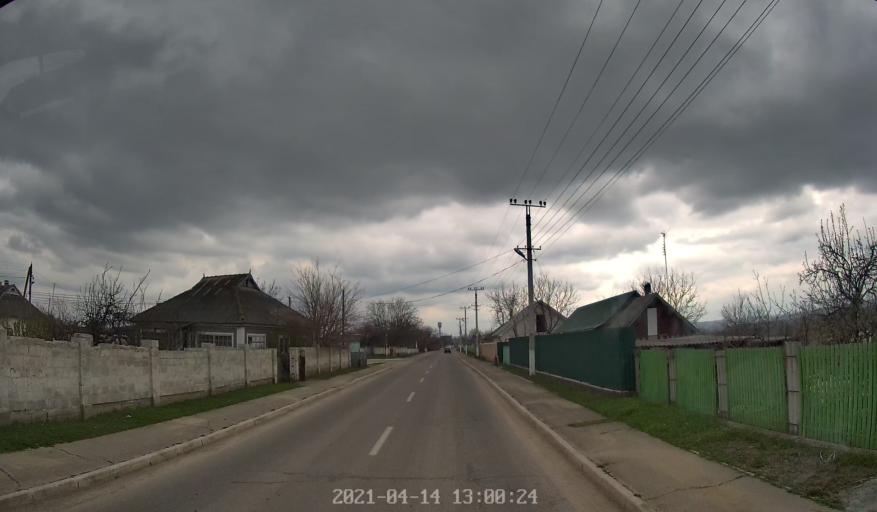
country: MD
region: Chisinau
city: Vadul lui Voda
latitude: 47.1390
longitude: 29.1213
